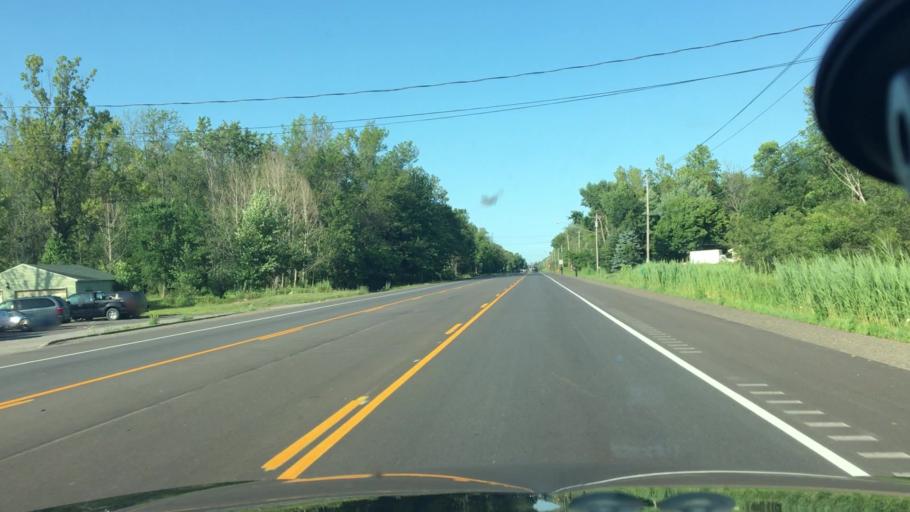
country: US
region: New York
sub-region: Erie County
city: Wanakah
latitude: 42.7153
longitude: -78.9076
